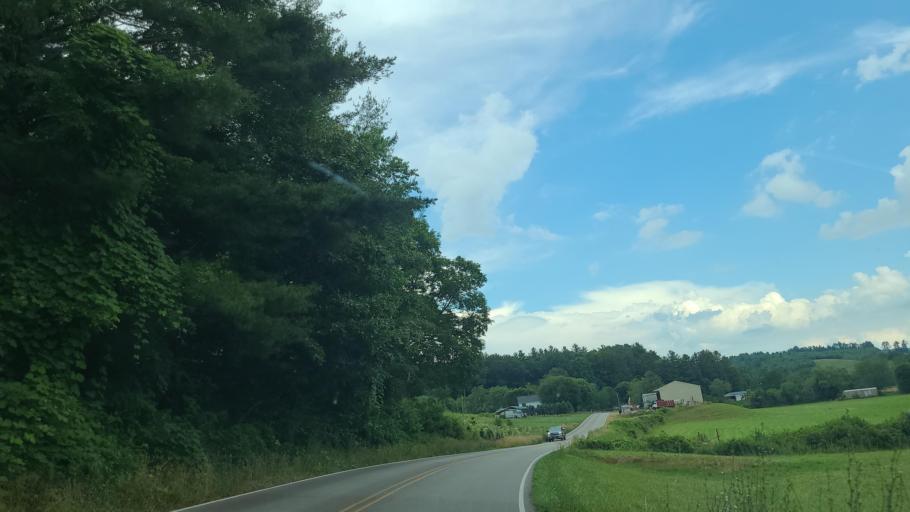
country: US
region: North Carolina
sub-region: Alleghany County
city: Sparta
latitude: 36.4187
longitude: -81.2701
